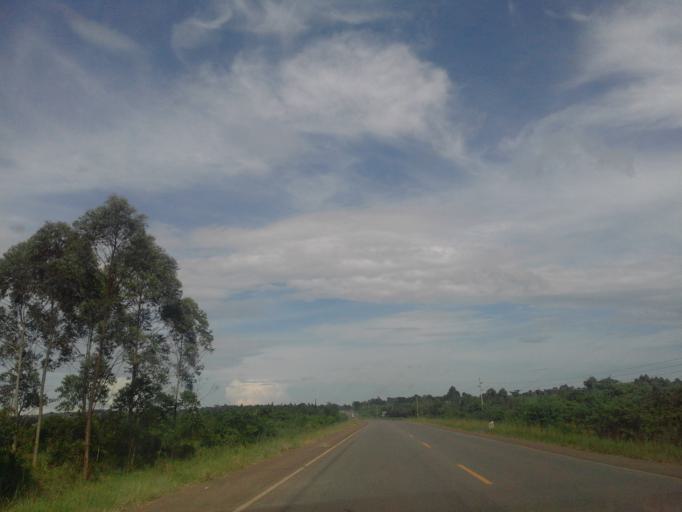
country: UG
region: Central Region
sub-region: Lwengo District
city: Lwengo
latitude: -0.3715
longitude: 31.5260
